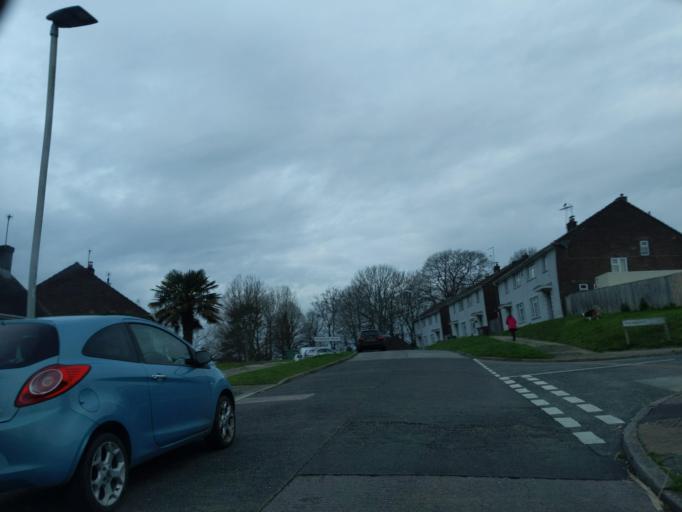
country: GB
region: England
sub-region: Plymouth
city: Plymouth
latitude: 50.4033
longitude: -4.1365
